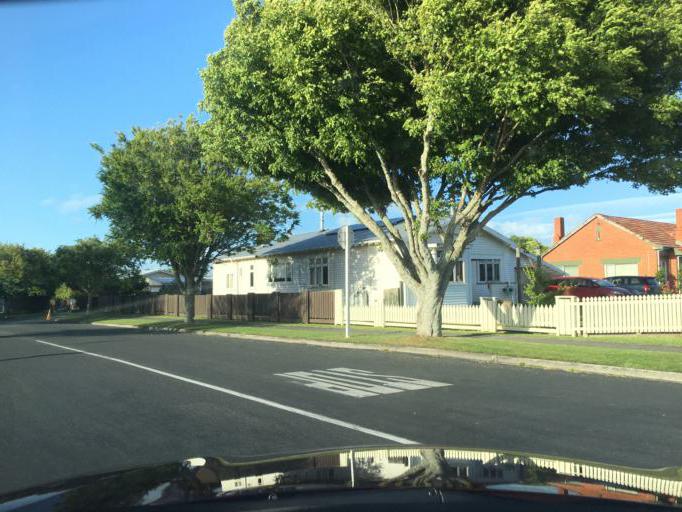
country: NZ
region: Waikato
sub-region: Waipa District
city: Cambridge
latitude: -38.0070
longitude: 175.3363
